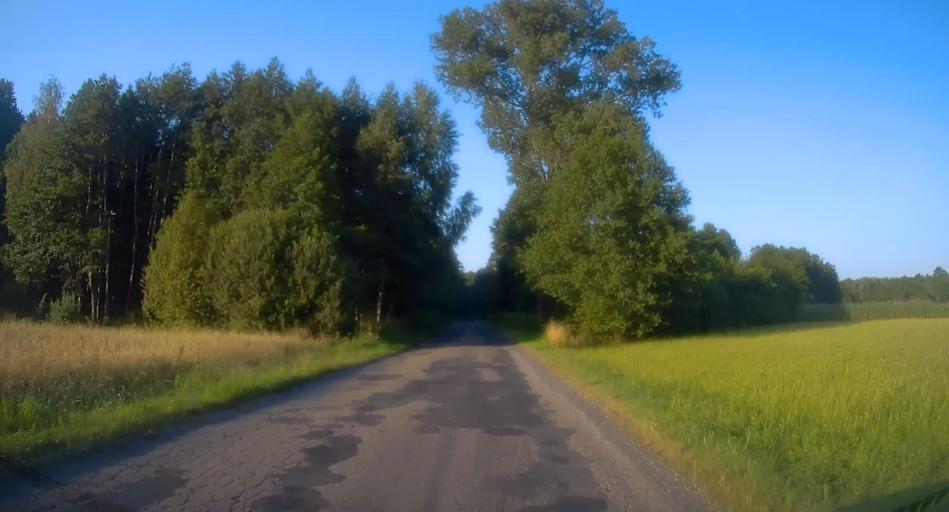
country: PL
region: Lodz Voivodeship
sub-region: Powiat skierniewicki
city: Kaweczyn Nowy
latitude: 51.8897
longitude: 20.2911
